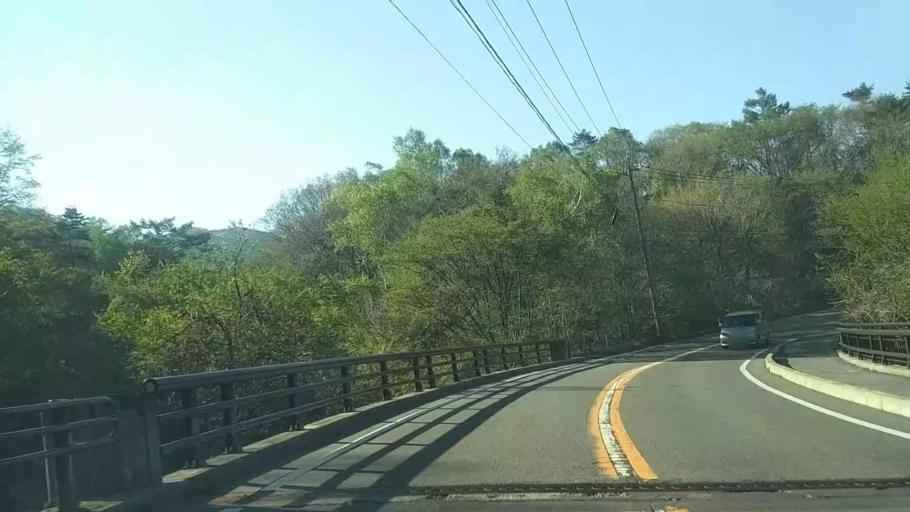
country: JP
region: Yamanashi
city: Nirasaki
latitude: 35.9215
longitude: 138.4051
